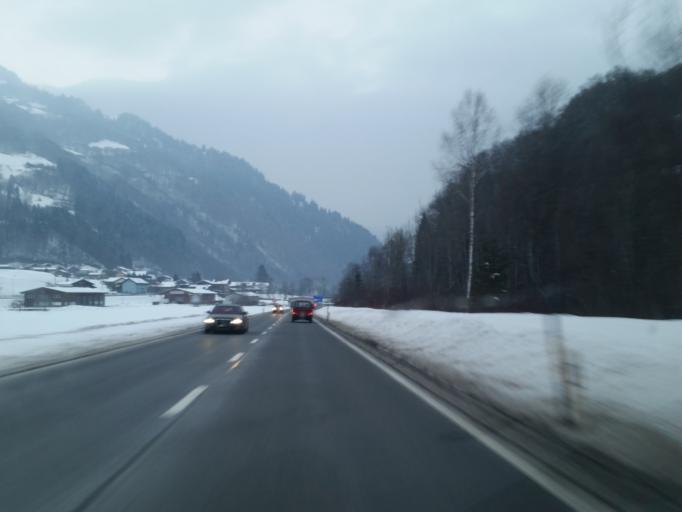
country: CH
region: Grisons
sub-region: Praettigau/Davos District
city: Jenaz
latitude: 46.9345
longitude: 9.7131
